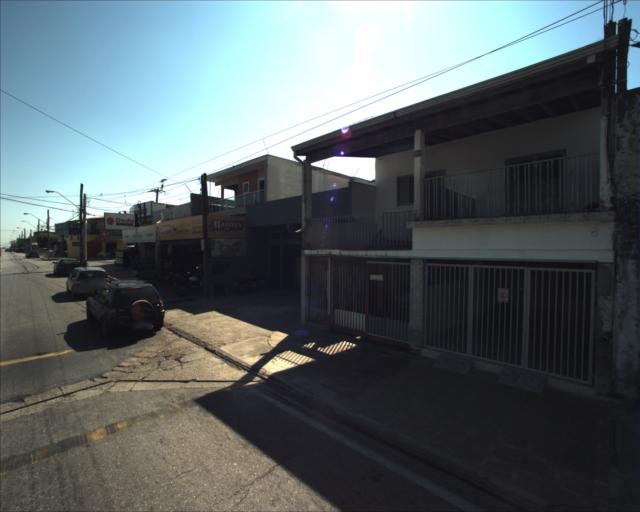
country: BR
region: Sao Paulo
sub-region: Sorocaba
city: Sorocaba
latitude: -23.4987
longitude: -47.5277
